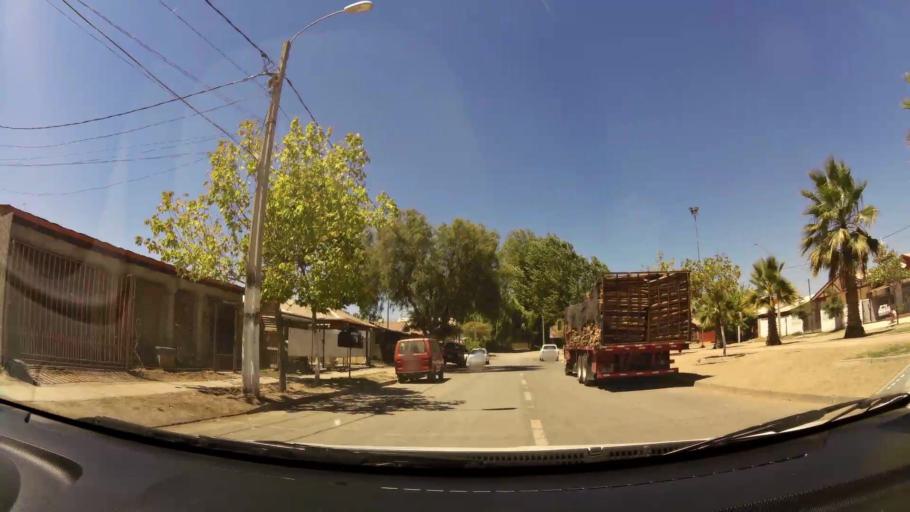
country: CL
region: O'Higgins
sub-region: Provincia de Cachapoal
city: Rancagua
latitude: -34.1659
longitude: -70.6968
